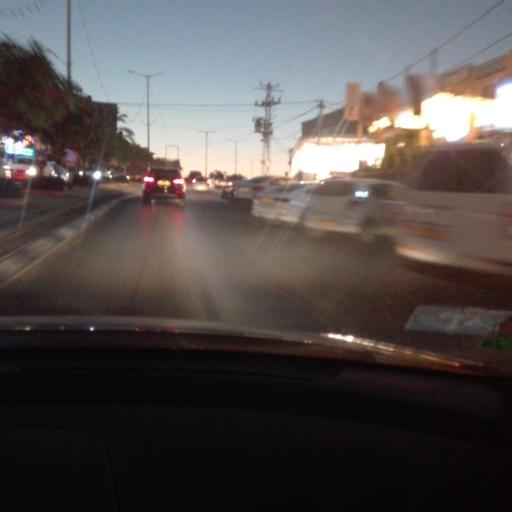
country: PS
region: West Bank
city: Nazlat `Isa
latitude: 32.4212
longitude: 35.0405
